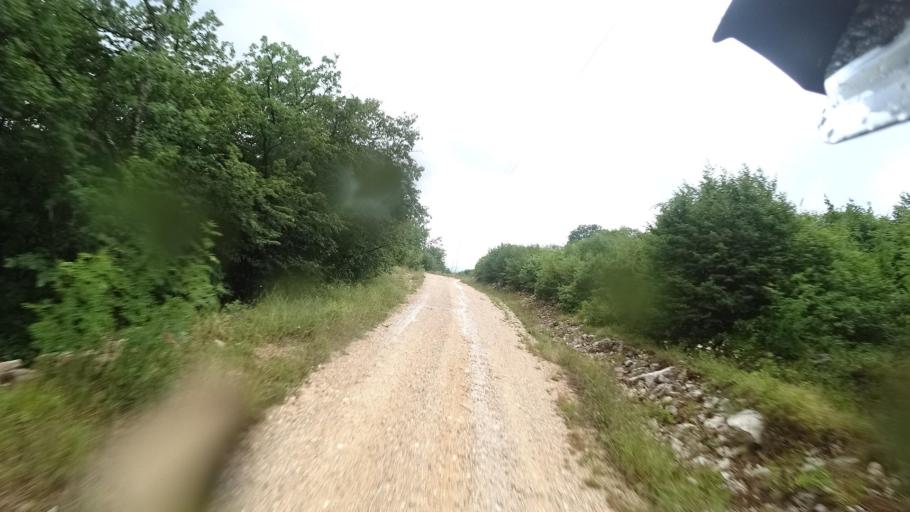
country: HR
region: Licko-Senjska
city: Jezerce
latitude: 44.7067
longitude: 15.6641
